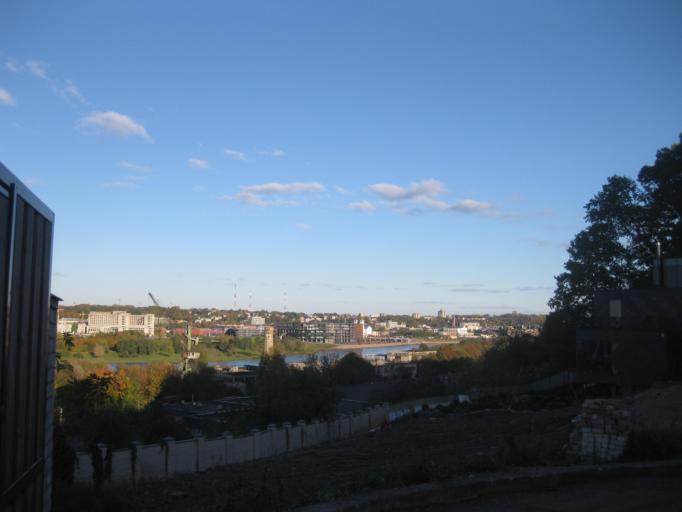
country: LT
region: Kauno apskritis
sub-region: Kaunas
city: Aleksotas
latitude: 54.8893
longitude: 23.8979
